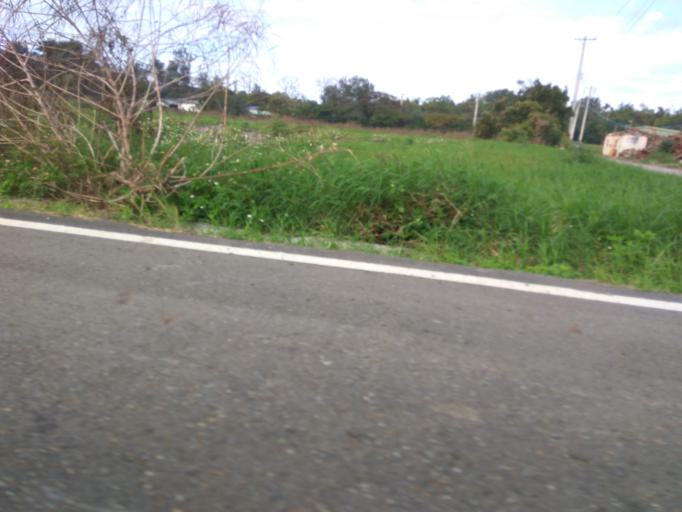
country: TW
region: Taiwan
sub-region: Hsinchu
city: Zhubei
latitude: 24.9607
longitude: 121.0068
